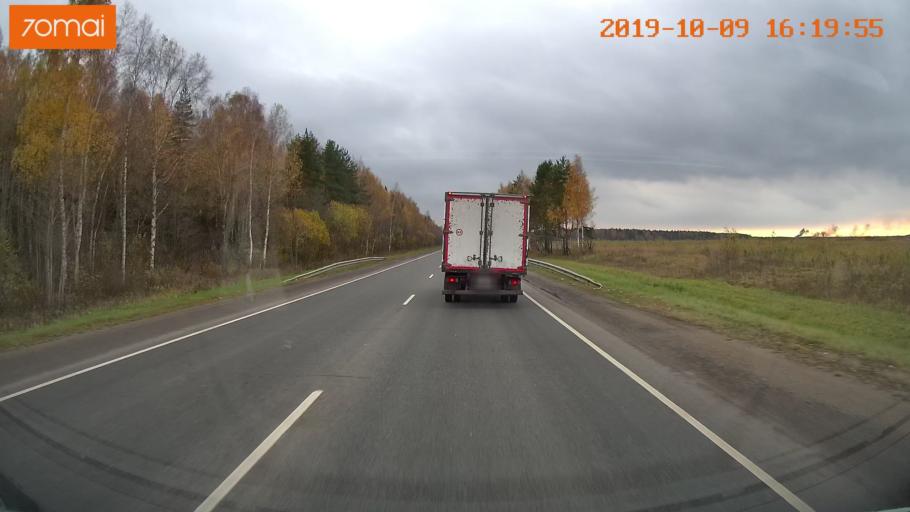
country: RU
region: Kostroma
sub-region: Kostromskoy Rayon
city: Kostroma
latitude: 57.7131
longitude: 40.8935
